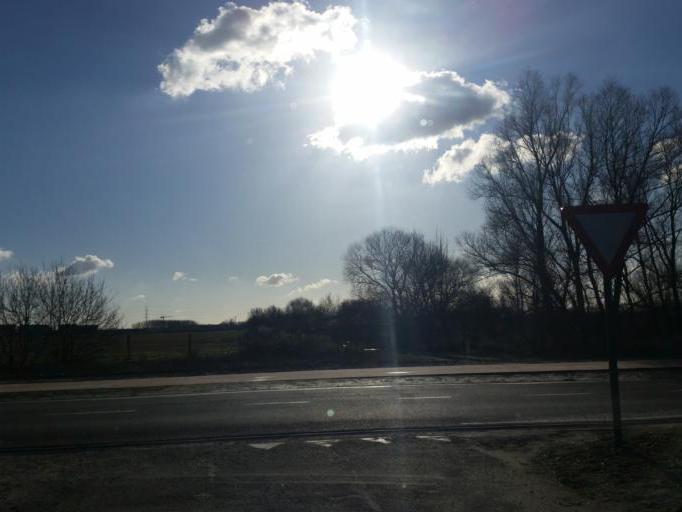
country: BE
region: Flanders
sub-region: Provincie Antwerpen
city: Zwijndrecht
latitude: 51.2498
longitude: 4.2972
